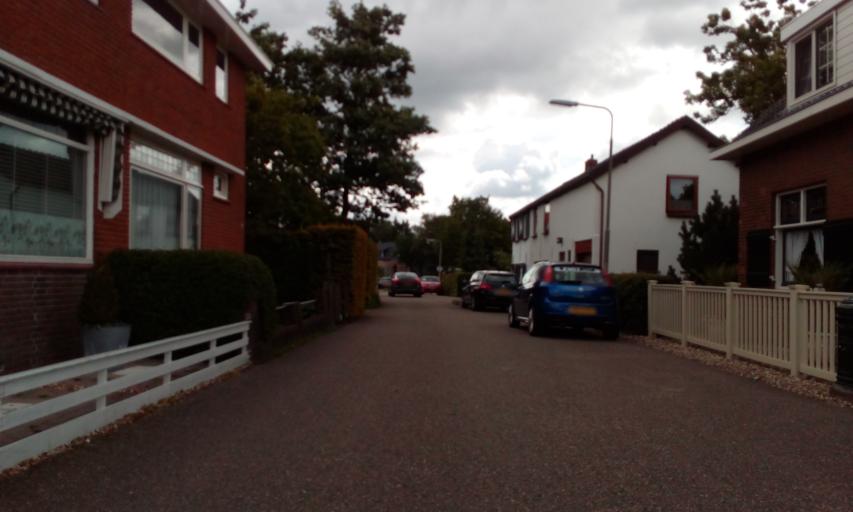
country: NL
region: South Holland
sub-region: Gemeente Barendrecht
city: Barendrecht
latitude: 51.8680
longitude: 4.5443
